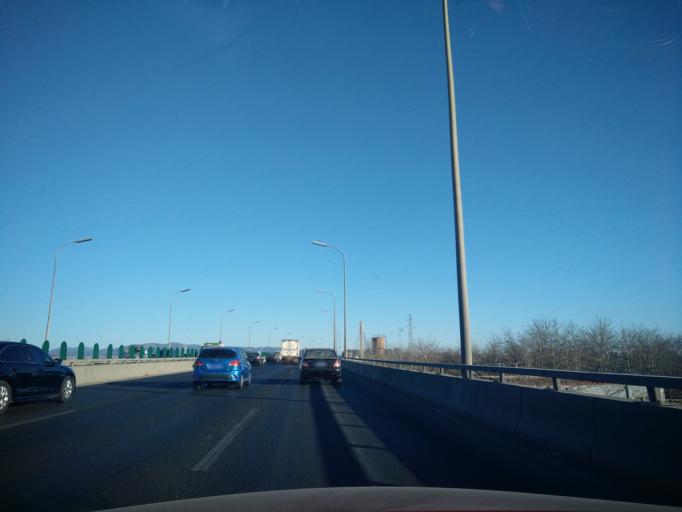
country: CN
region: Beijing
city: Lugu
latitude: 39.8746
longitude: 116.2021
